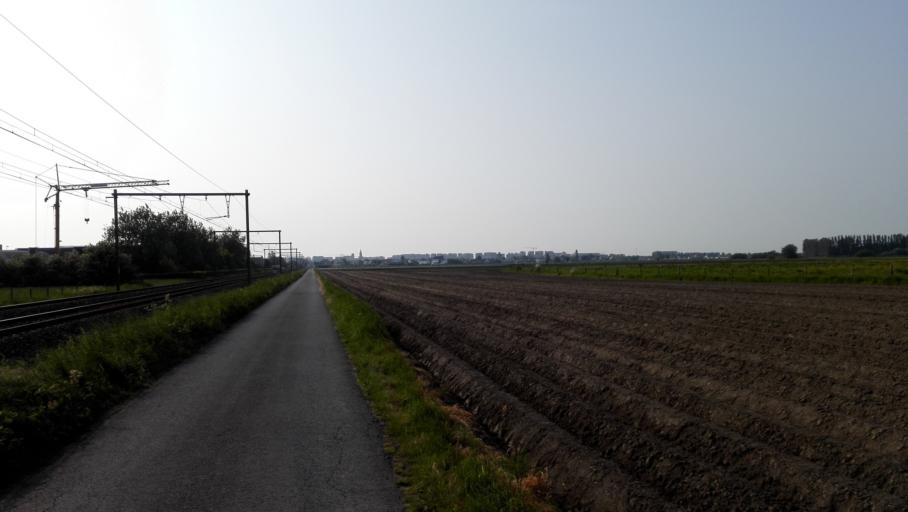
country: BE
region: Flanders
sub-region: Provincie West-Vlaanderen
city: Zuienkerke
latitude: 51.2965
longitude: 3.1594
